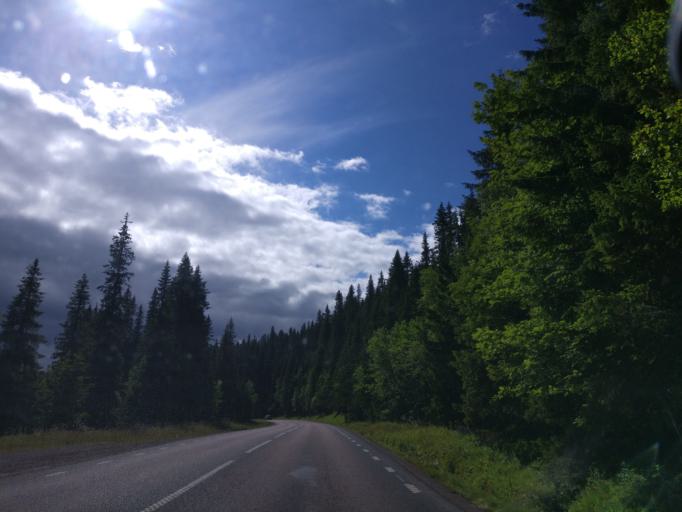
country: SE
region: Dalarna
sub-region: Malung-Saelens kommun
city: Malung
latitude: 61.1672
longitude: 13.1531
